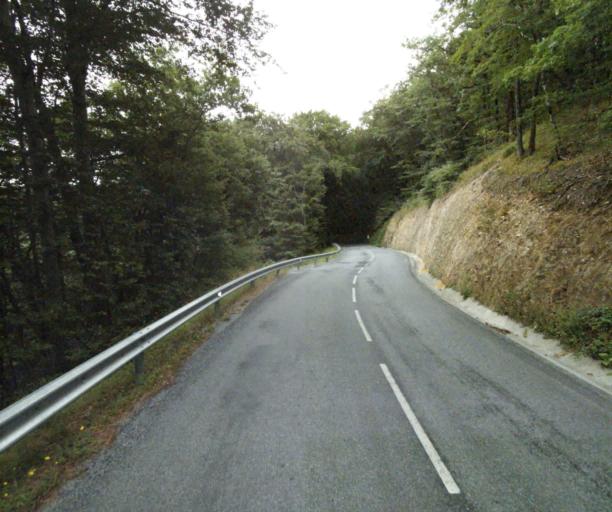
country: FR
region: Midi-Pyrenees
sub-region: Departement du Tarn
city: Soreze
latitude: 43.4368
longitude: 2.0879
